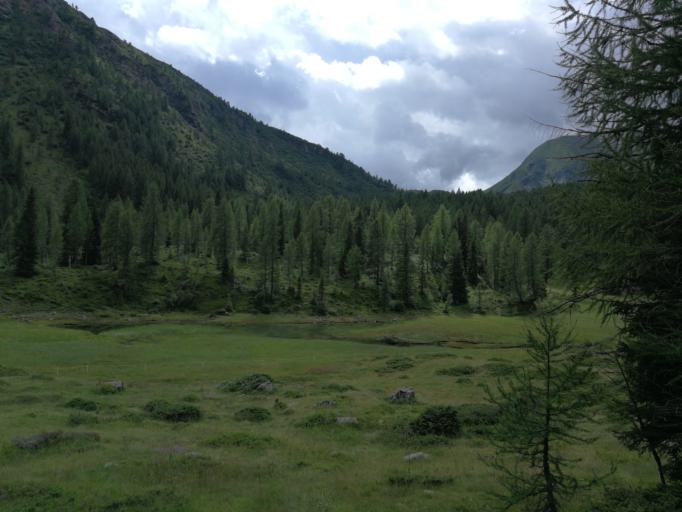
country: IT
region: Trentino-Alto Adige
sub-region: Provincia di Trento
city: Brione
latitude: 45.9321
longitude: 10.5363
